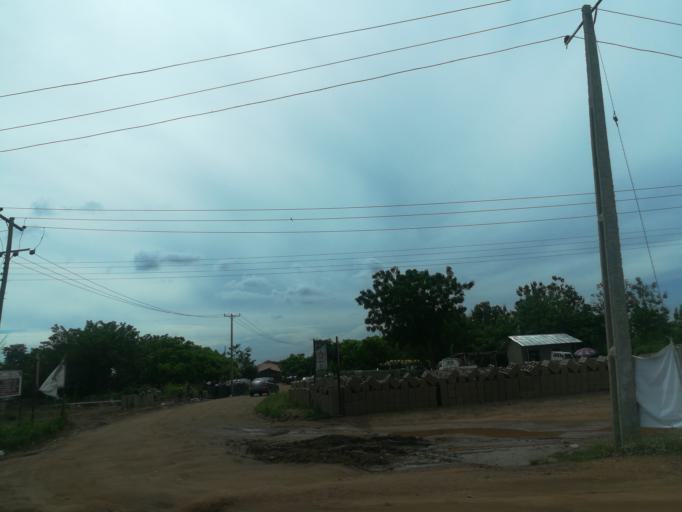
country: NG
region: Oyo
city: Ibadan
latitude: 7.3676
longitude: 3.9762
